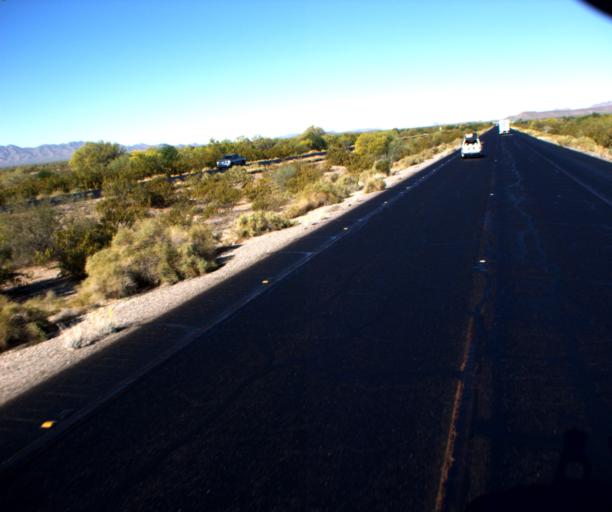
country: US
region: Arizona
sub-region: Pinal County
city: Maricopa
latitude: 32.8407
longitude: -112.2425
